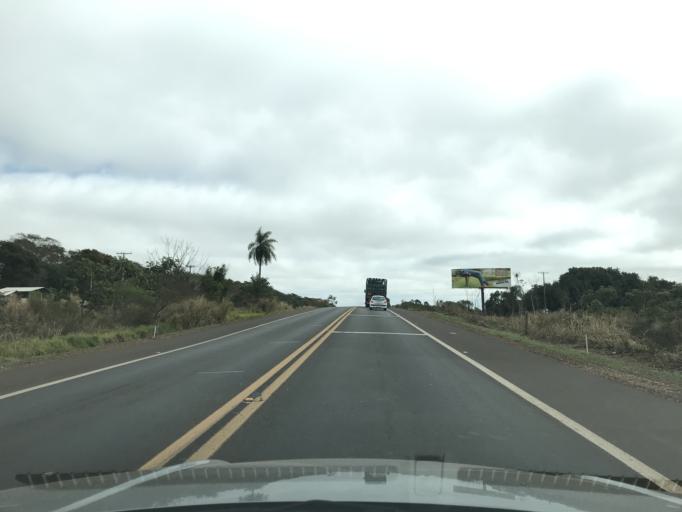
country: PY
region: Canindeyu
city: Salto del Guaira
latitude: -24.0083
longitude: -54.3085
